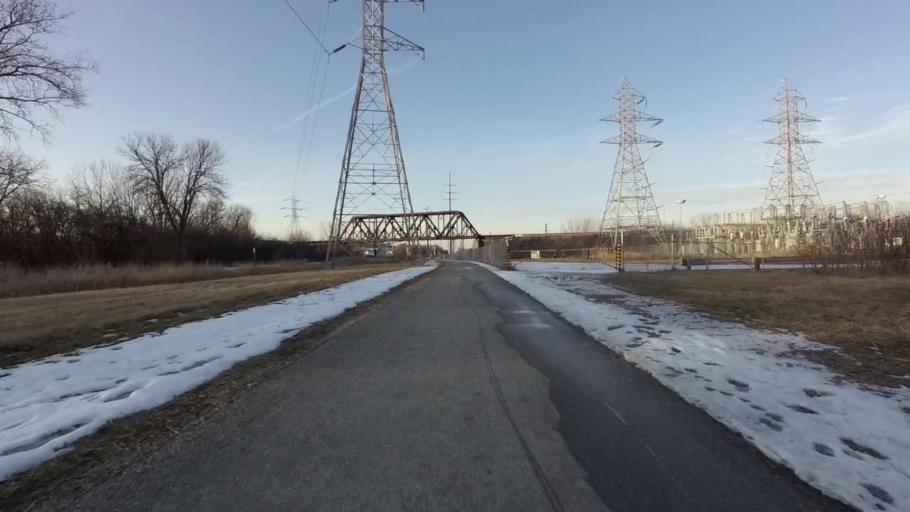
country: US
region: Wisconsin
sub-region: Milwaukee County
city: Glendale
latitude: 43.1309
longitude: -87.9468
